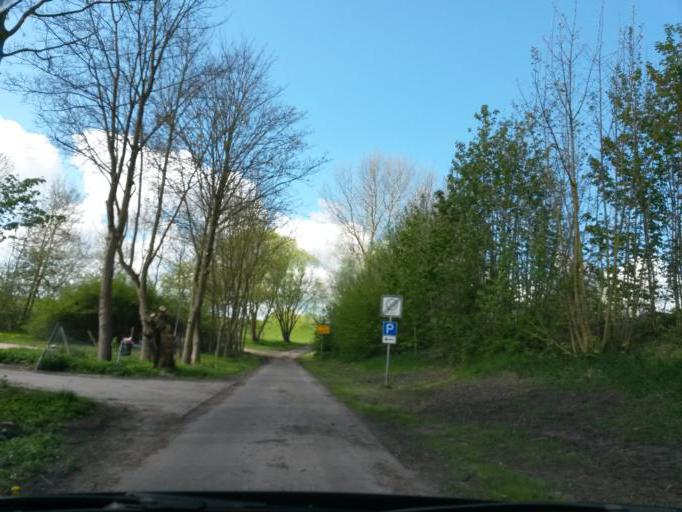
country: DE
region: Schleswig-Holstein
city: Haseldorf
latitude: 53.6486
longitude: 9.5601
